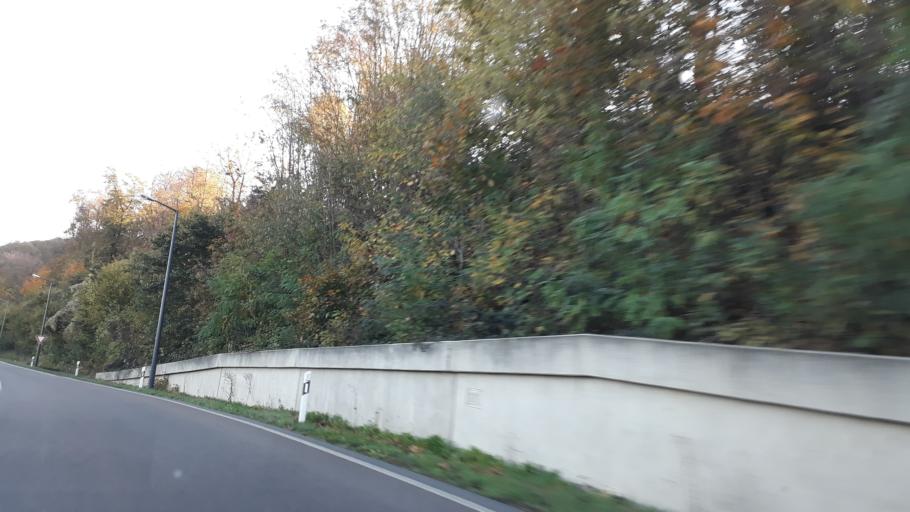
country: DE
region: Saxony
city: Coswig
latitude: 51.0921
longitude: 13.6060
